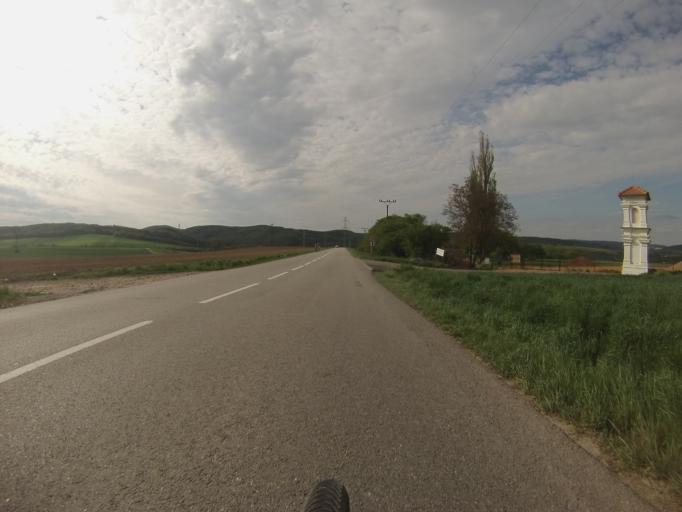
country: CZ
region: South Moravian
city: Veverska Bityska
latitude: 49.2605
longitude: 16.4444
